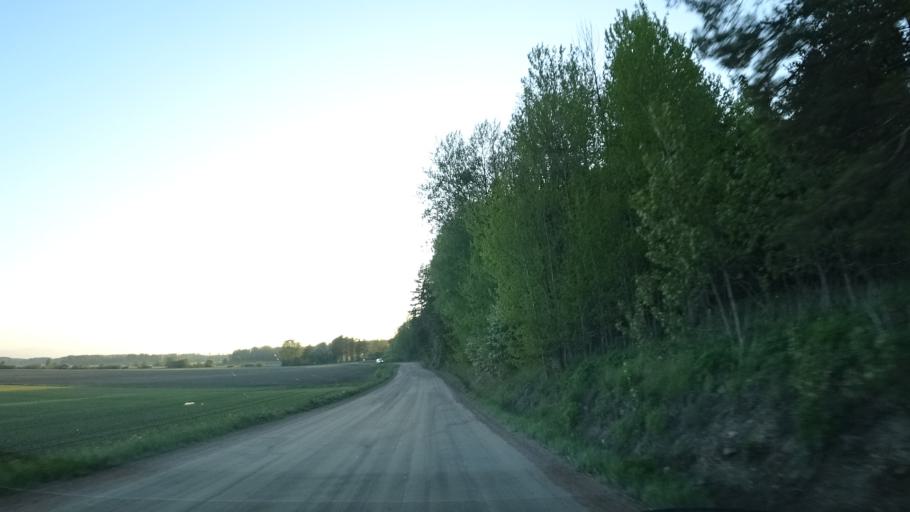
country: FI
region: Uusimaa
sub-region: Helsinki
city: Siuntio
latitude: 60.0795
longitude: 24.1908
